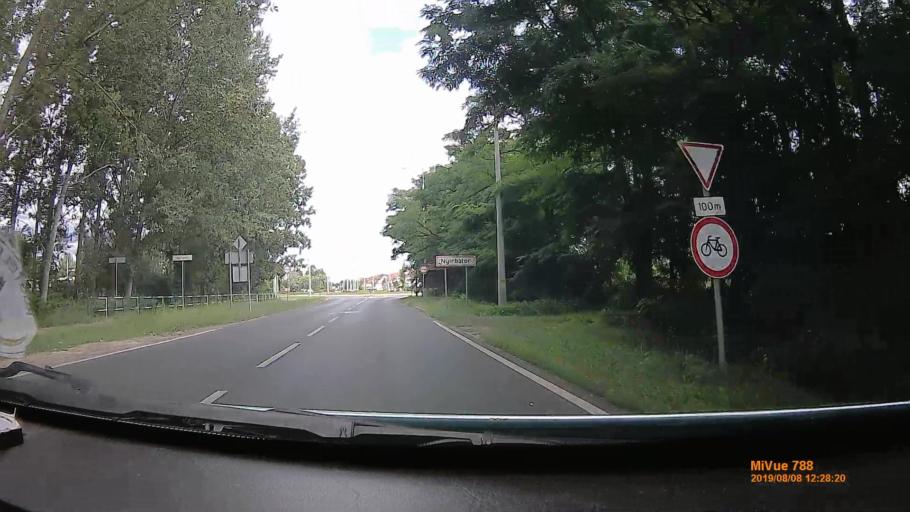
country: HU
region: Szabolcs-Szatmar-Bereg
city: Nyirbator
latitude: 47.8290
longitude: 22.1119
